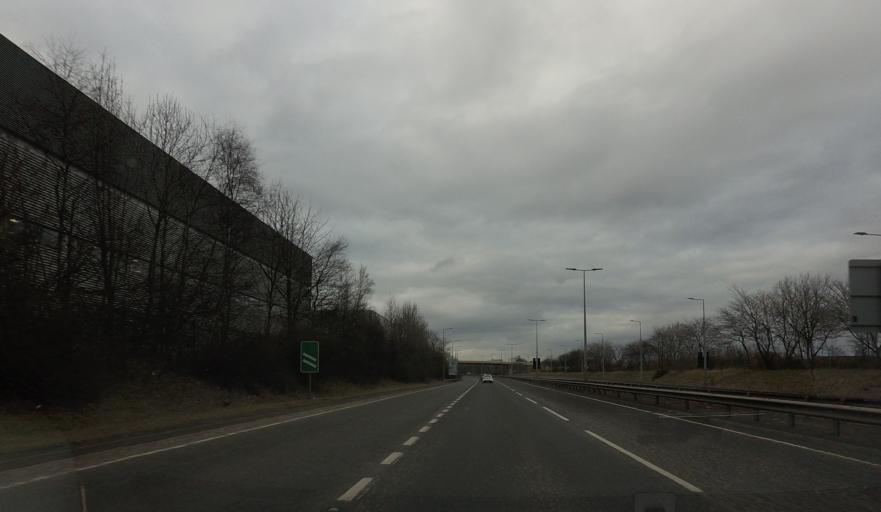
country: GB
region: Scotland
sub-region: Highland
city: Inverness
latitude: 57.4767
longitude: -4.1880
